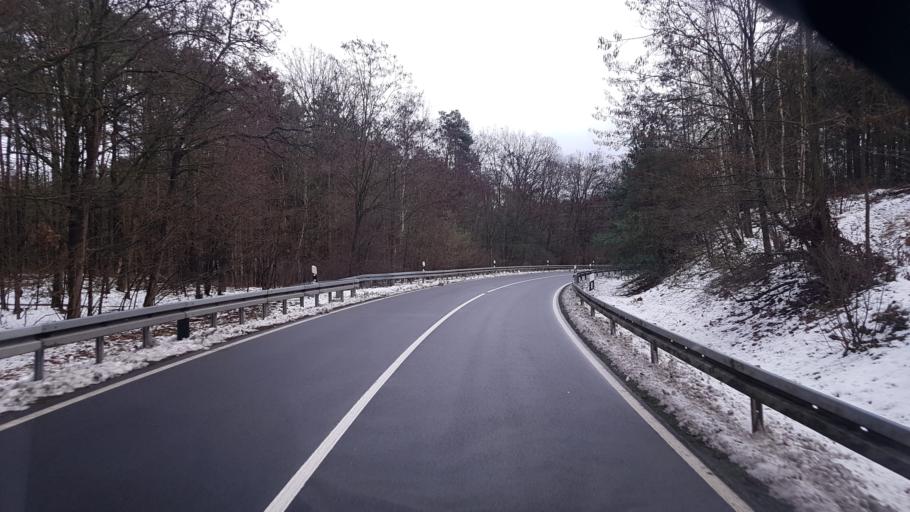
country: DE
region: Brandenburg
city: Schenkendobern
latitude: 51.9759
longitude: 14.5513
